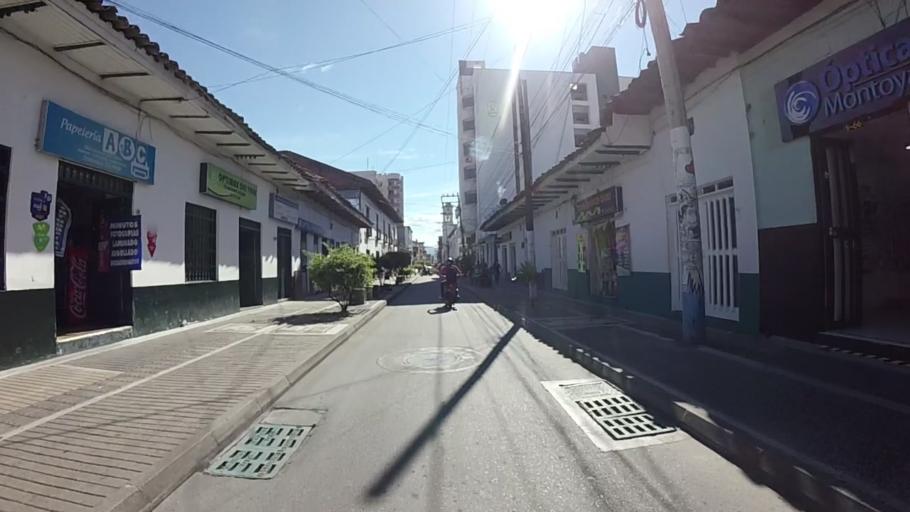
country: CO
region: Valle del Cauca
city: Cartago
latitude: 4.7503
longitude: -75.9100
